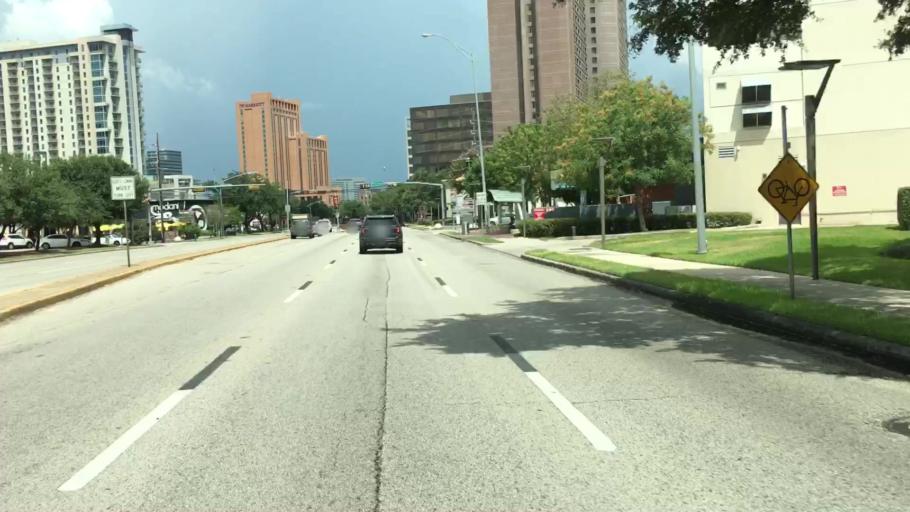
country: US
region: Texas
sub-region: Harris County
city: Bellaire
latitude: 29.7388
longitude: -95.4716
